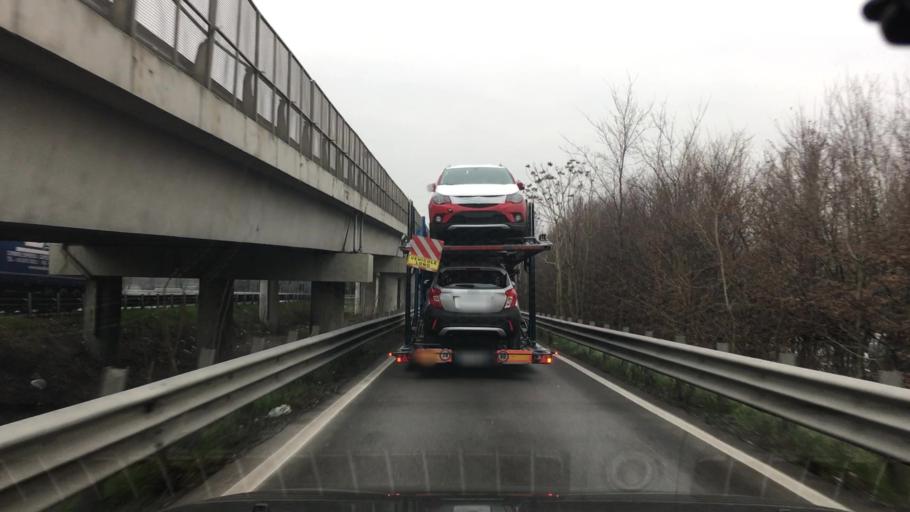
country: IT
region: Emilia-Romagna
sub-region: Provincia di Reggio Emilia
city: Reggio nell'Emilia
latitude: 44.7192
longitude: 10.6242
